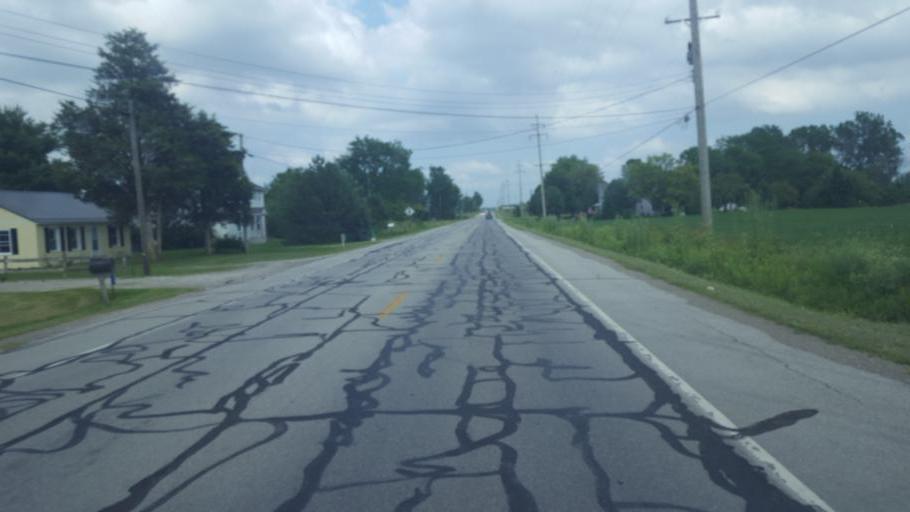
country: US
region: Ohio
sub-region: Crawford County
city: Crestline
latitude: 40.7869
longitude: -82.7137
